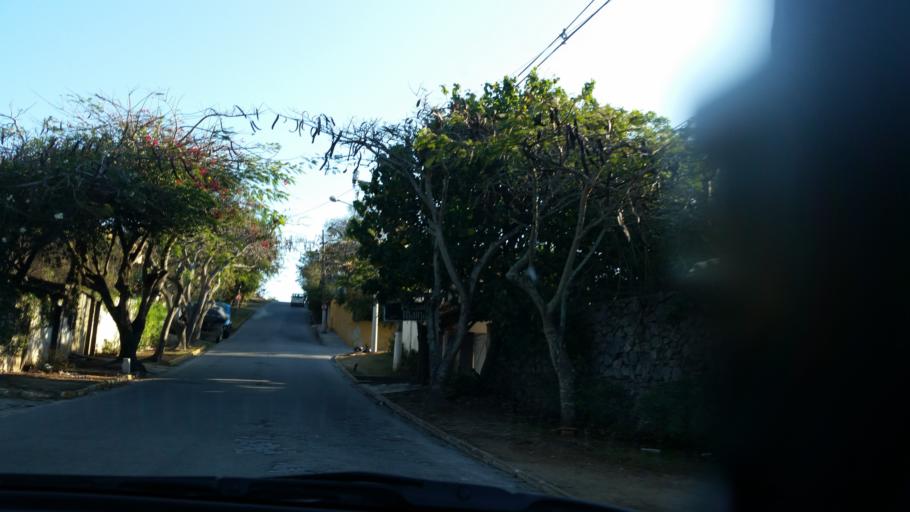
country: BR
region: Rio de Janeiro
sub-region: Armacao De Buzios
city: Armacao de Buzios
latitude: -22.7472
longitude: -41.8791
